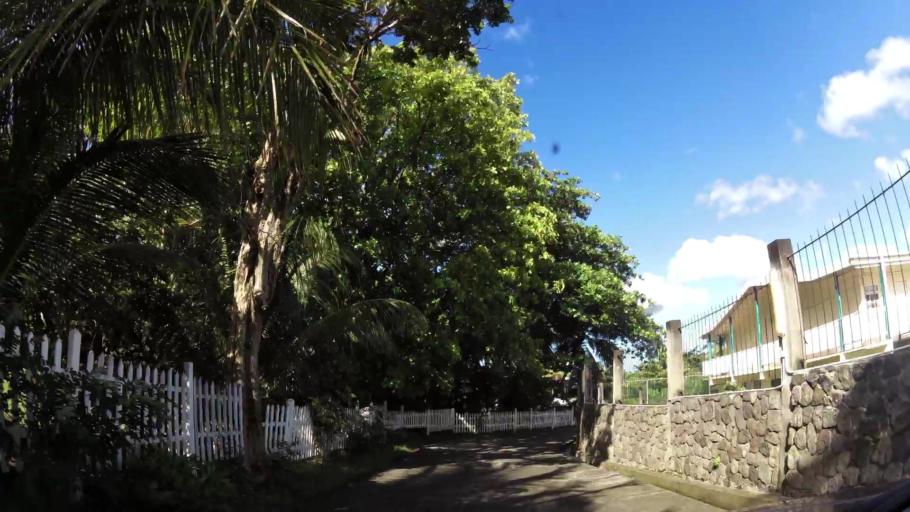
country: DM
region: Saint John
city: Portsmouth
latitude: 15.5537
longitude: -61.4611
